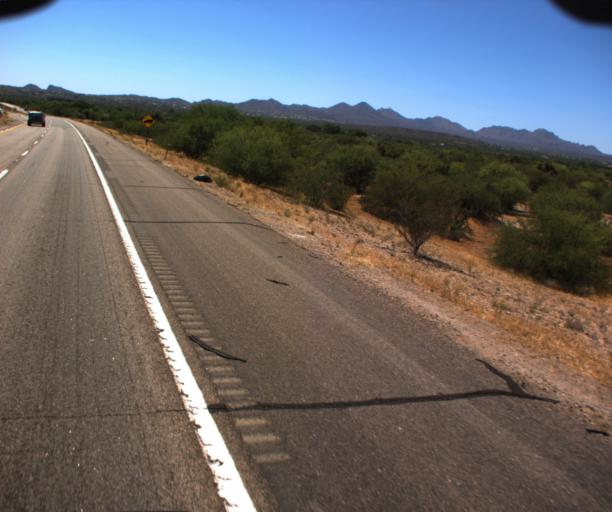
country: US
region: Arizona
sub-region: Maricopa County
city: Fountain Hills
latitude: 33.5826
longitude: -111.6596
